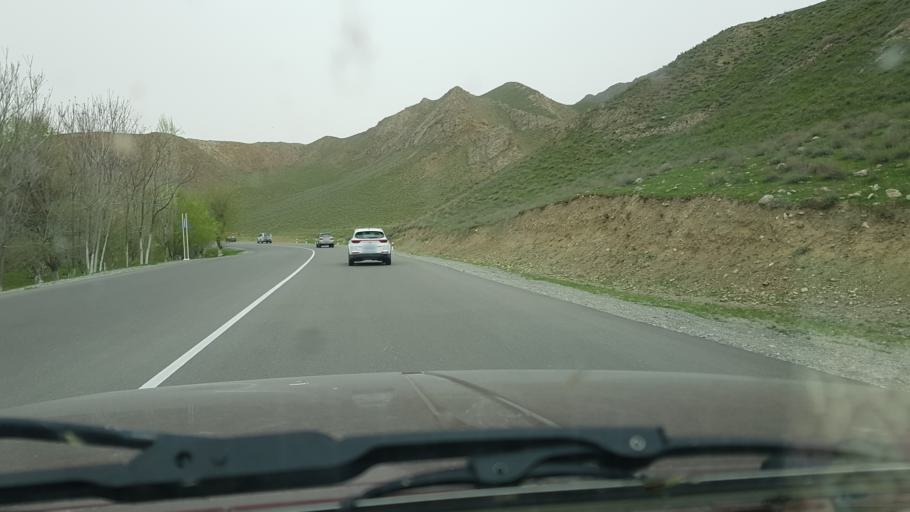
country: TM
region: Ahal
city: Arcabil
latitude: 38.0176
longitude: 58.0061
